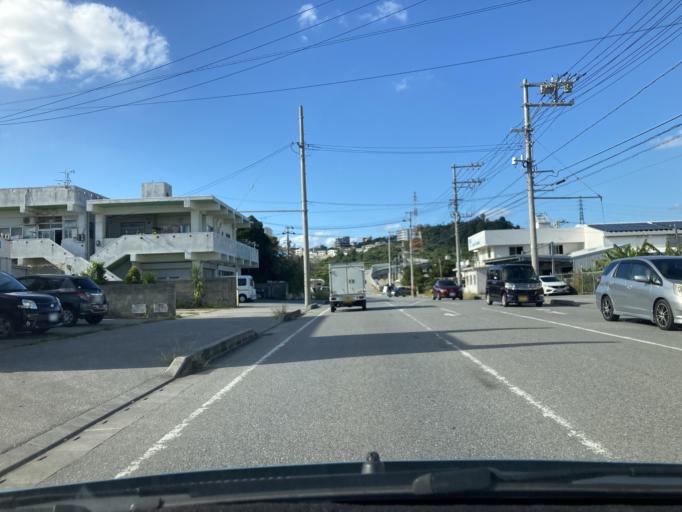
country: JP
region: Okinawa
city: Okinawa
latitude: 26.3353
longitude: 127.8368
